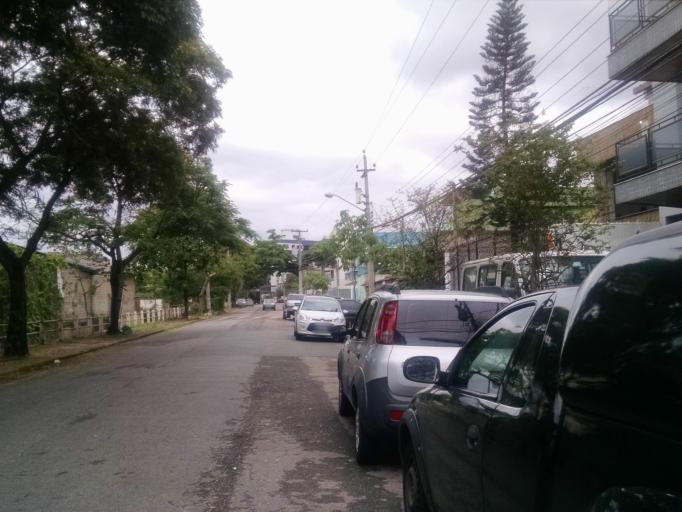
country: BR
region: Rio de Janeiro
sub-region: Duque De Caxias
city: Duque de Caxias
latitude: -22.8354
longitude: -43.3107
